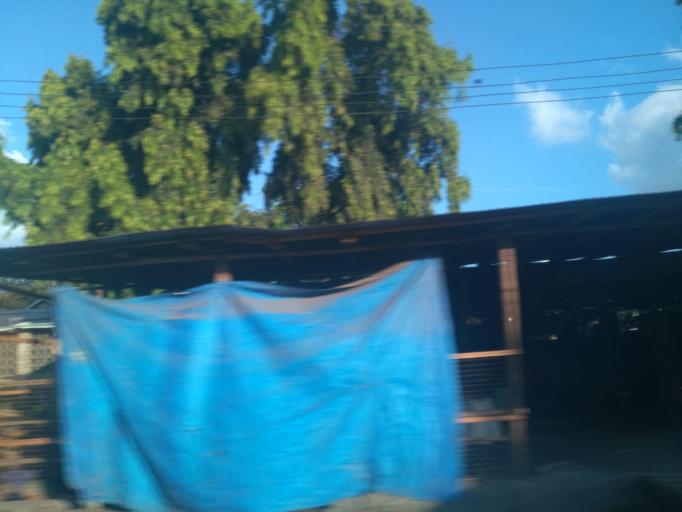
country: TZ
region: Dar es Salaam
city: Dar es Salaam
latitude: -6.8603
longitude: 39.2601
